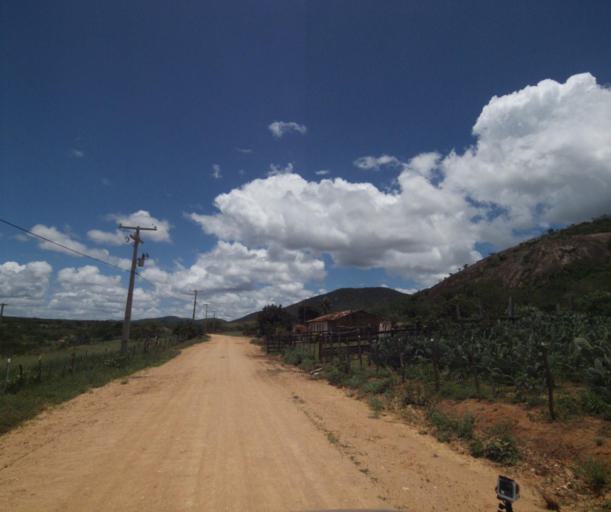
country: BR
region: Bahia
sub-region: Pocoes
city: Pocoes
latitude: -14.3856
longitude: -40.4251
